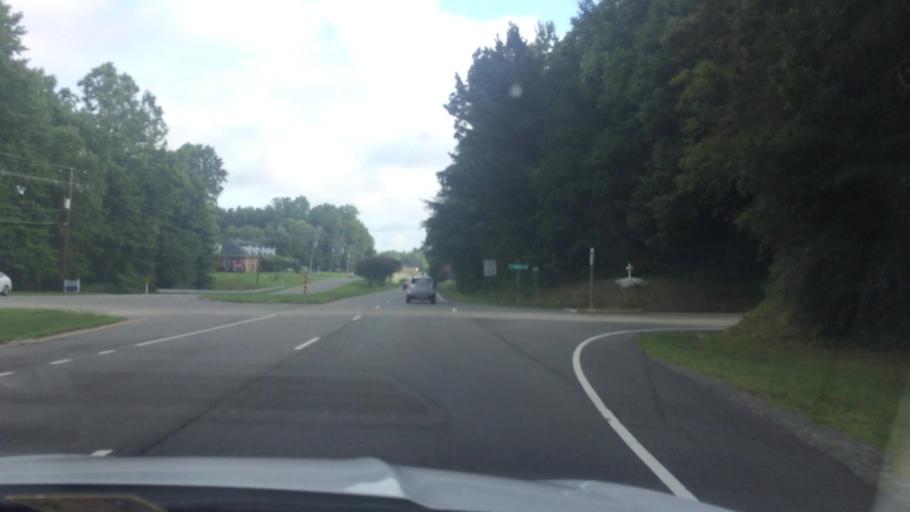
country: US
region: Virginia
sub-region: Gloucester County
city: Gloucester Courthouse
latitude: 37.4022
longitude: -76.5192
